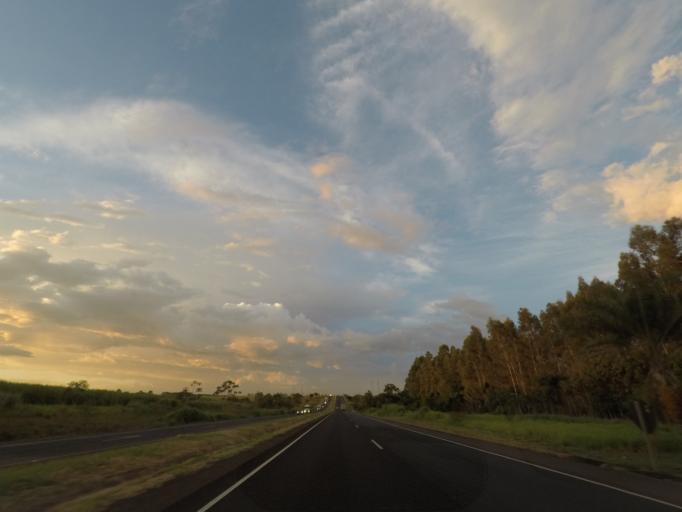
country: BR
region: Minas Gerais
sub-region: Uberaba
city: Uberaba
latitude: -19.6579
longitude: -48.0031
